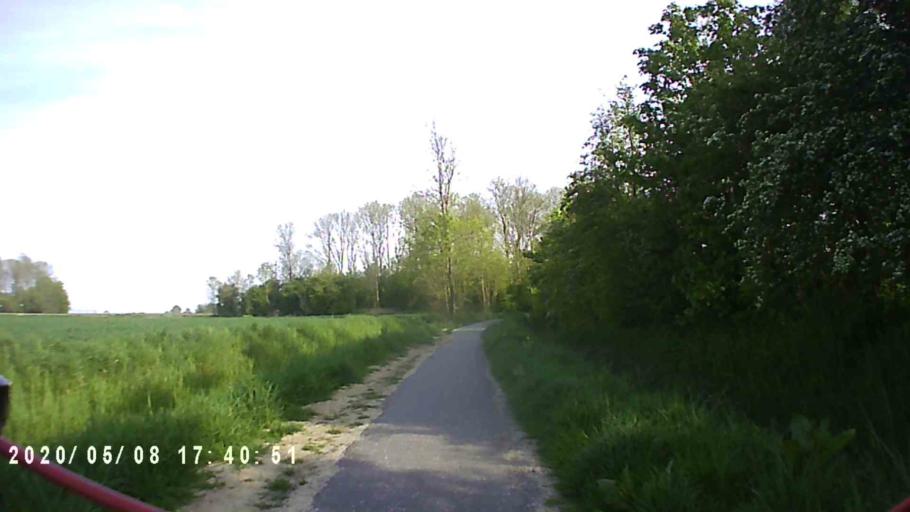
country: NL
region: Groningen
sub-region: Gemeente Winsum
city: Winsum
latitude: 53.3694
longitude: 6.5194
